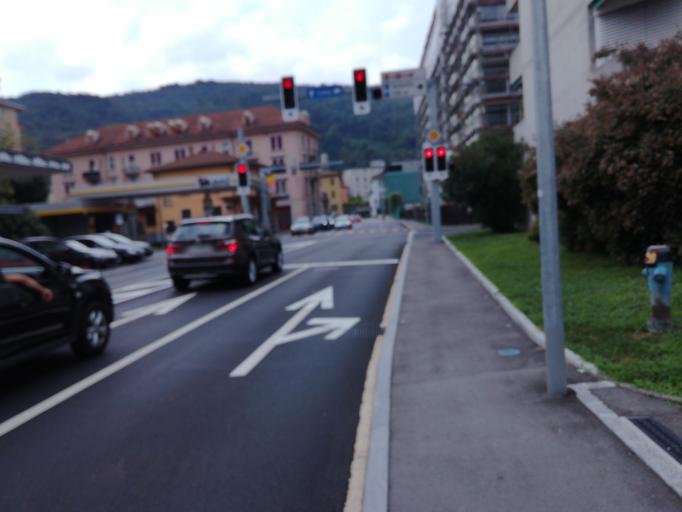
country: CH
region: Ticino
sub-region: Mendrisio District
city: Chiasso
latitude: 45.8342
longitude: 9.0348
